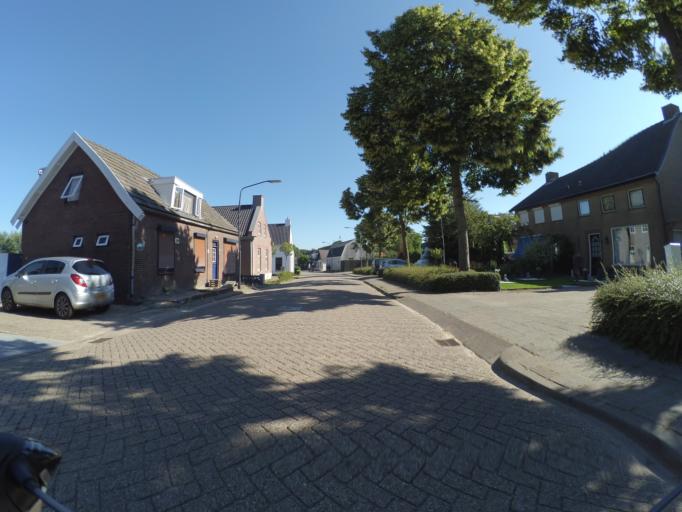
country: NL
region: North Brabant
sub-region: Gemeente Made en Drimmelen
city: Made
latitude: 51.6551
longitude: 4.8099
